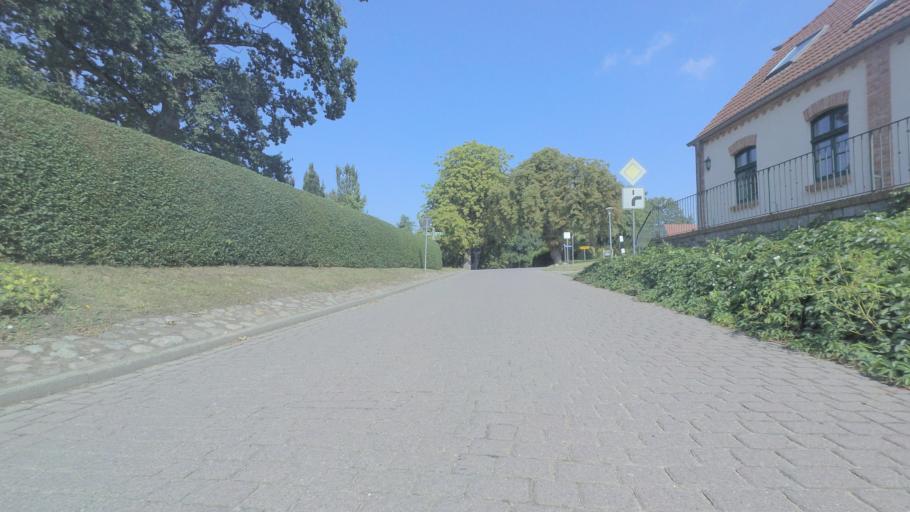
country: DE
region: Mecklenburg-Vorpommern
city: Pampow
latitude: 53.6828
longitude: 12.5663
